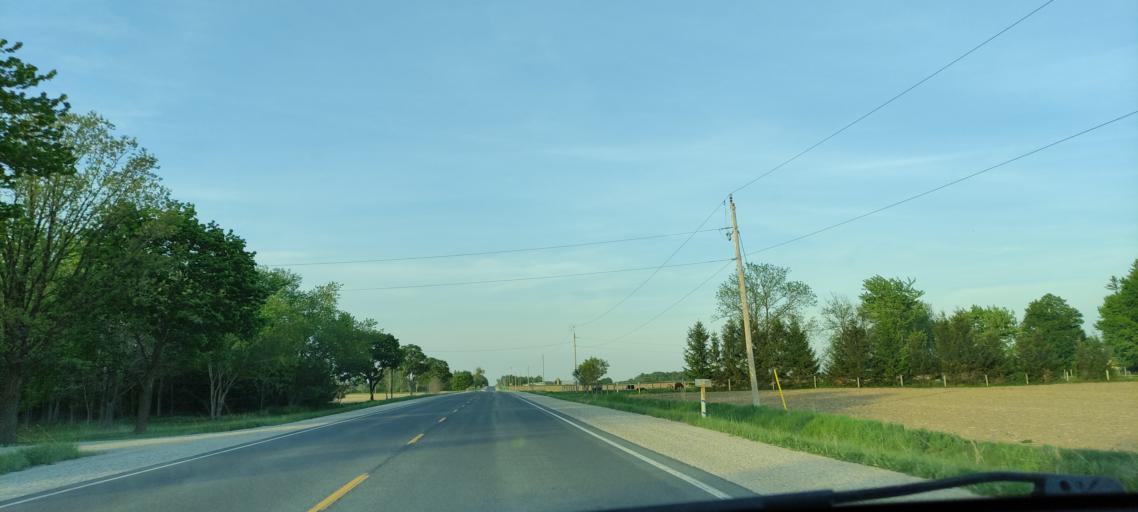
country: CA
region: Ontario
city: London
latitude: 43.2136
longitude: -81.1901
